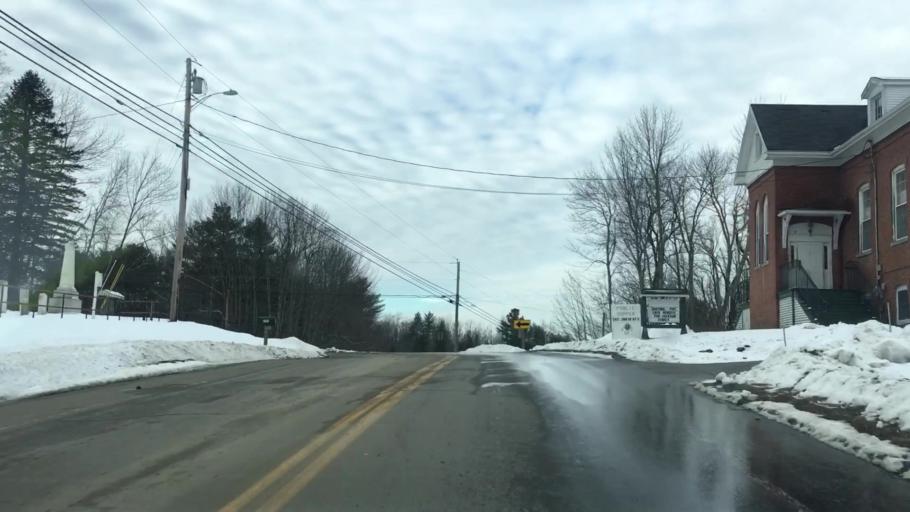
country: US
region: Maine
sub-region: Lincoln County
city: Whitefield
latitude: 44.2287
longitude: -69.6130
